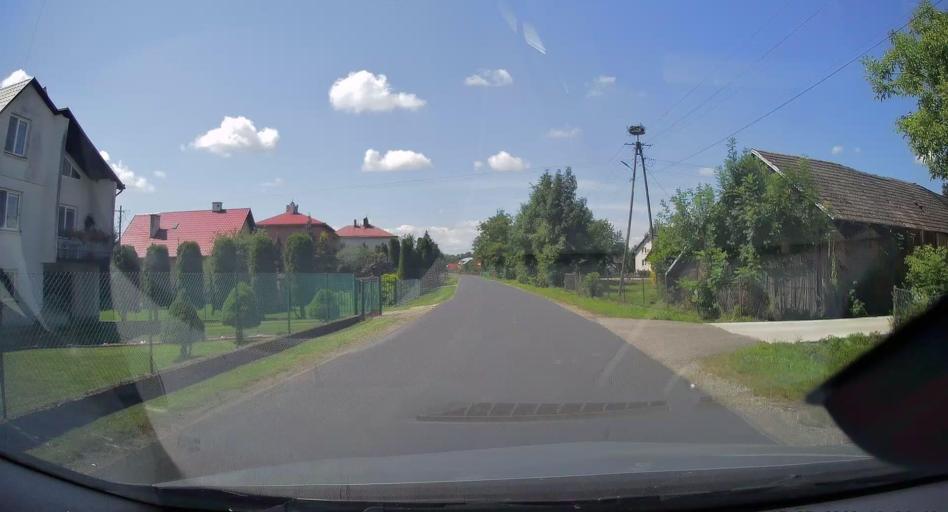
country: PL
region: Subcarpathian Voivodeship
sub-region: Powiat przemyski
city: Medyka
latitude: 49.8345
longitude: 22.8787
